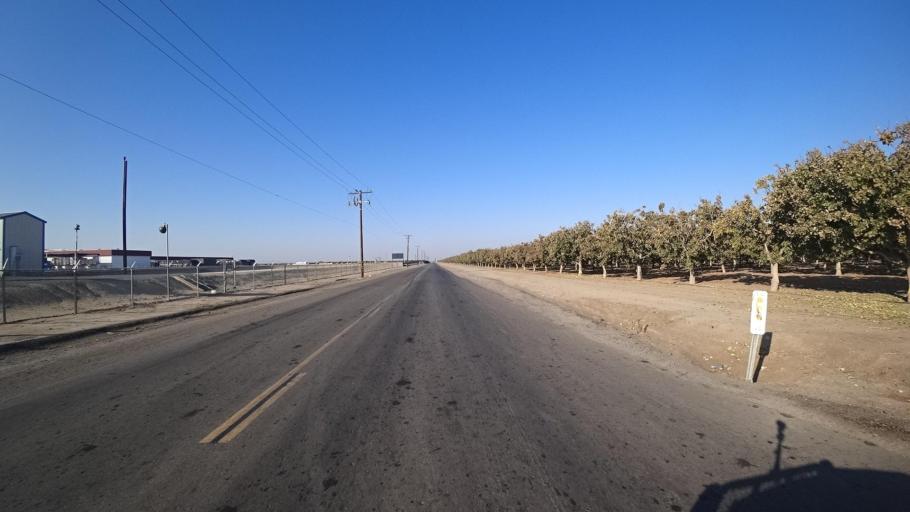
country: US
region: California
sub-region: Tulare County
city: Richgrove
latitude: 35.7906
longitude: -119.1611
